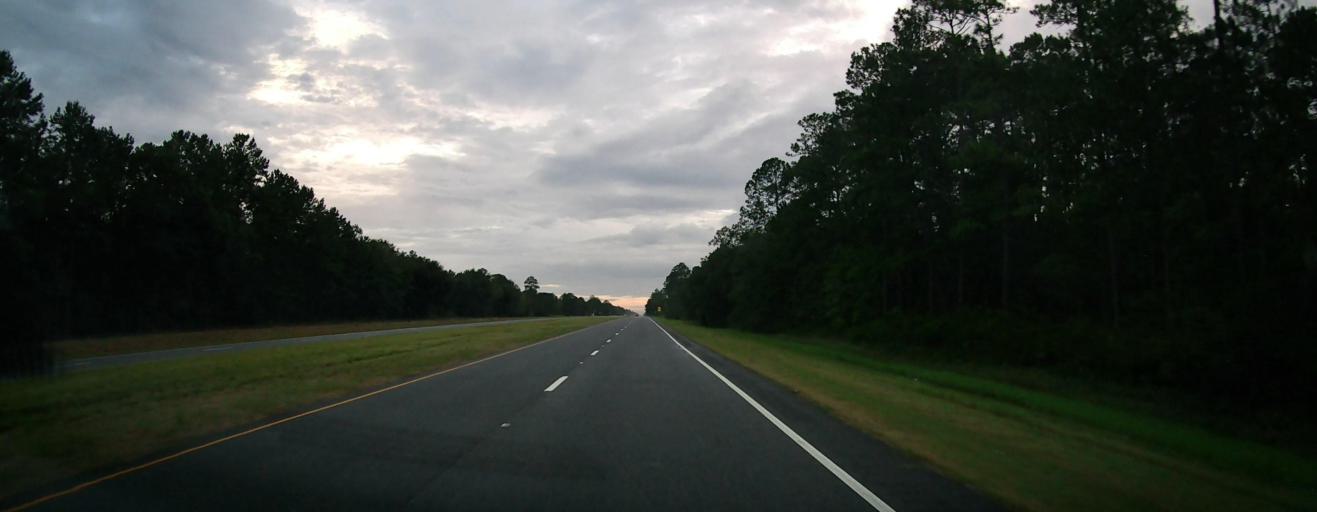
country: US
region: Georgia
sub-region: Lanier County
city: Lakeland
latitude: 30.8943
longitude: -83.1144
